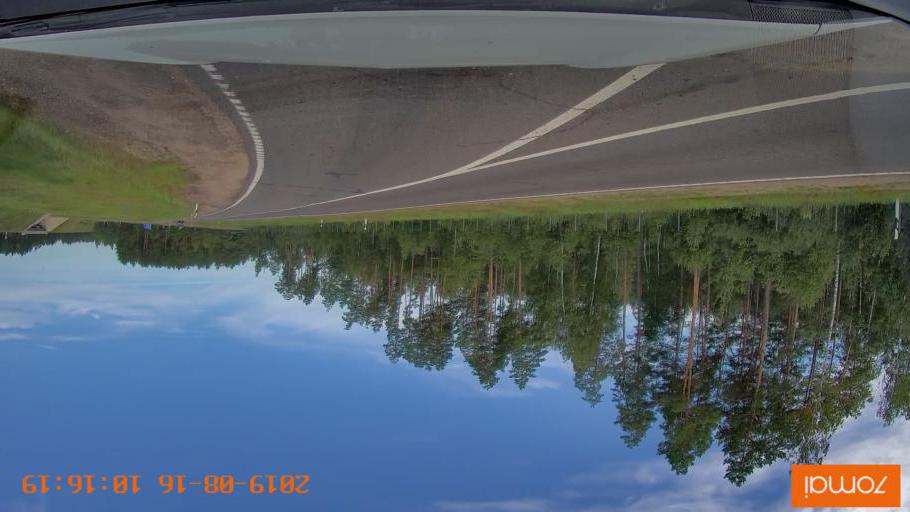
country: BY
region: Mogilev
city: Asipovichy
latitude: 53.3178
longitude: 28.7226
